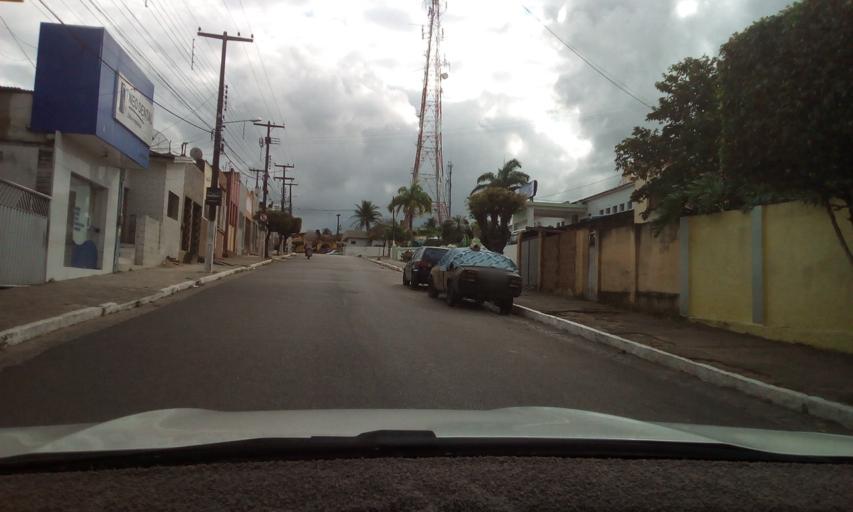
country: BR
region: Paraiba
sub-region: Mamanguape
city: Mamanguape
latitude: -6.8356
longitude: -35.1242
